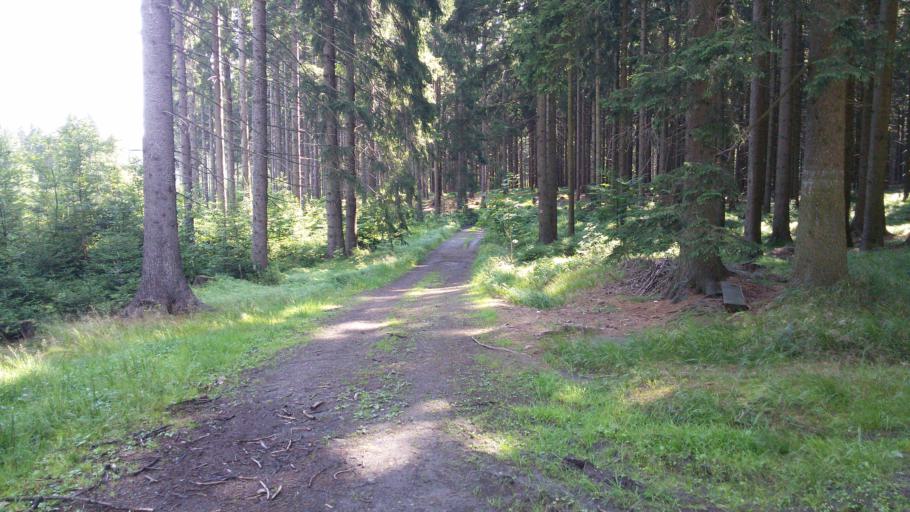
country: CZ
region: Vysocina
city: Heralec
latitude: 49.6539
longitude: 15.9695
